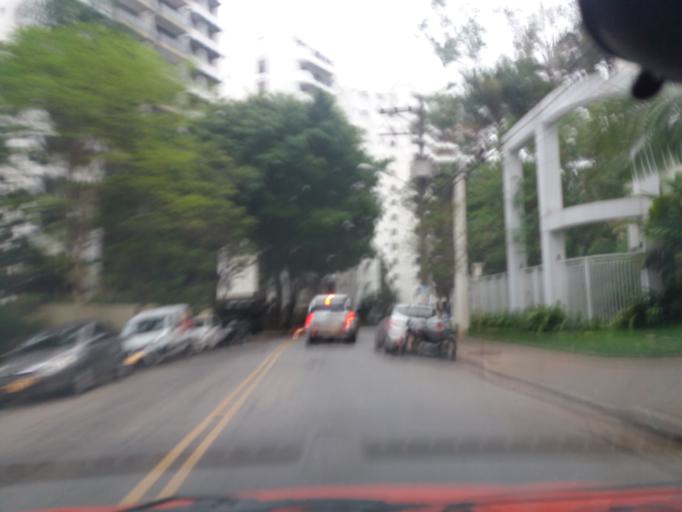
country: BR
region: Sao Paulo
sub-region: Taboao Da Serra
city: Taboao da Serra
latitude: -23.6240
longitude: -46.7350
